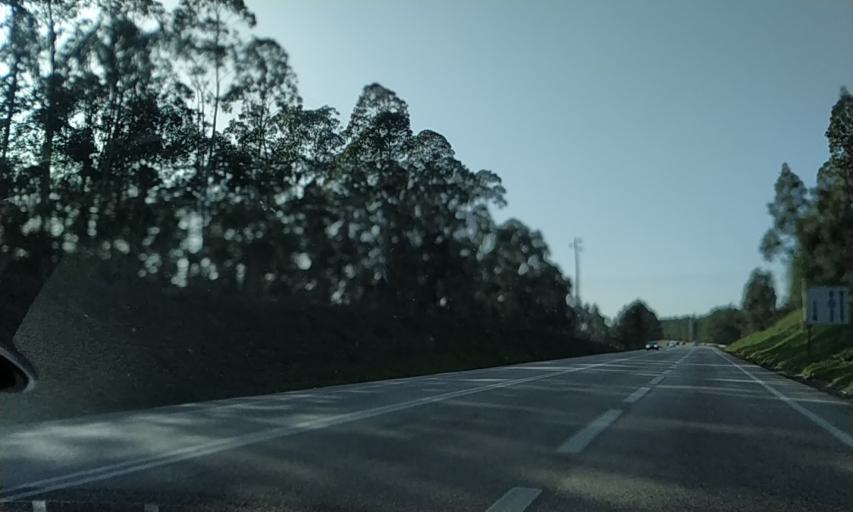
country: PT
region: Leiria
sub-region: Leiria
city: Leiria
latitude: 39.7462
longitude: -8.8521
